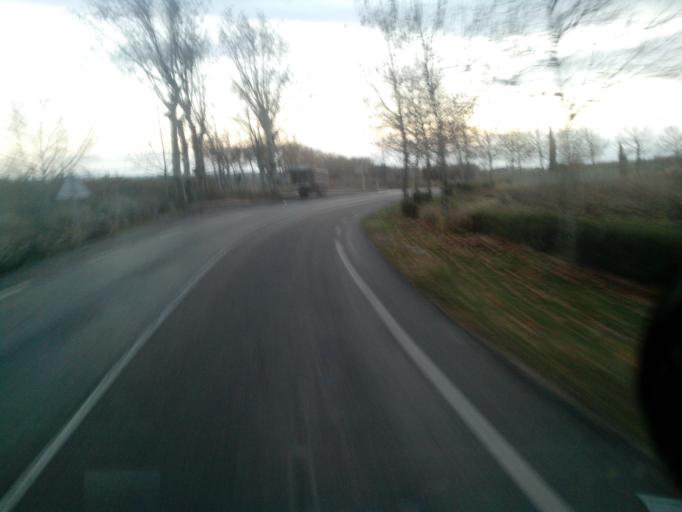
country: FR
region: Languedoc-Roussillon
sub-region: Departement de l'Herault
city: Aniane
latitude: 43.6794
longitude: 3.5782
